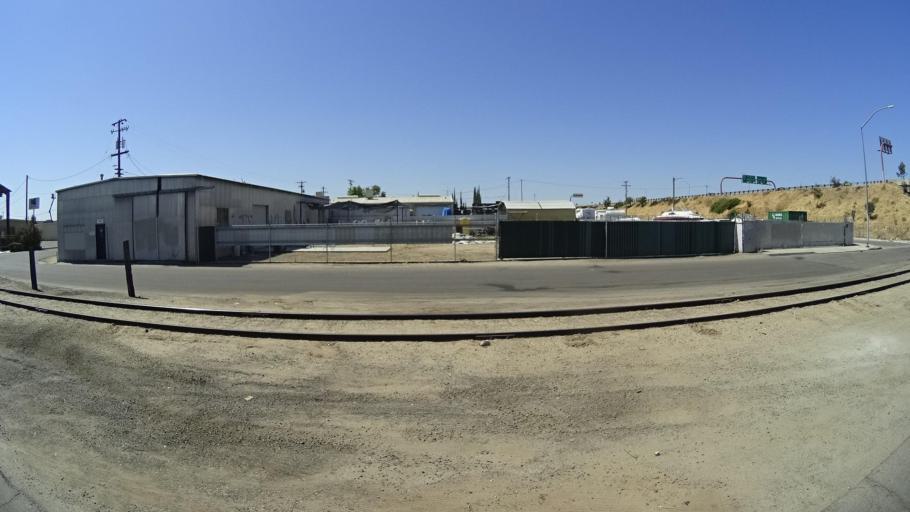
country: US
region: California
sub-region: Fresno County
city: Fresno
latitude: 36.7615
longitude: -119.7481
